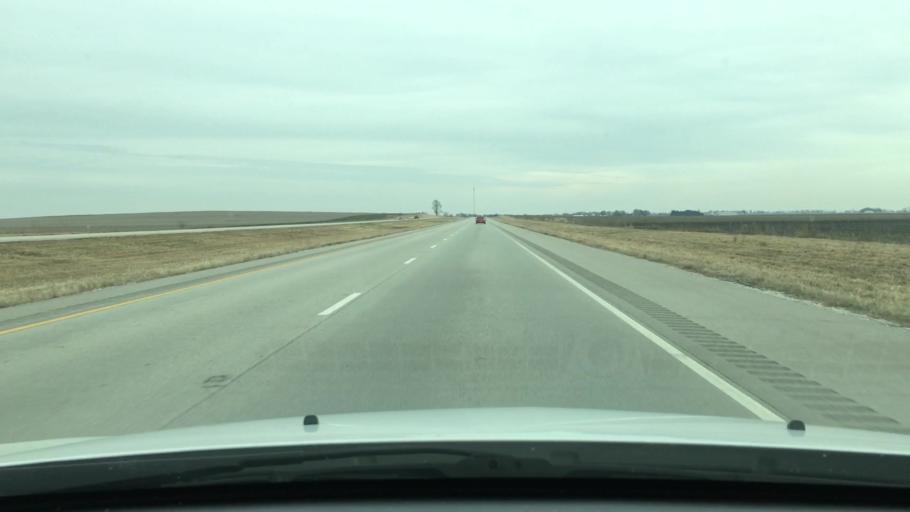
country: US
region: Illinois
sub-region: Morgan County
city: Jacksonville
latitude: 39.7384
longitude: -90.1047
